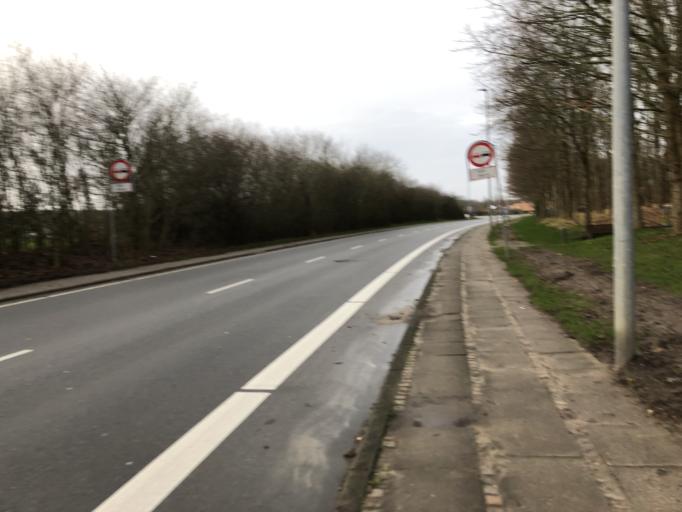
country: DK
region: Central Jutland
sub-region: Ringkobing-Skjern Kommune
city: Ringkobing
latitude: 56.0918
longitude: 8.2625
